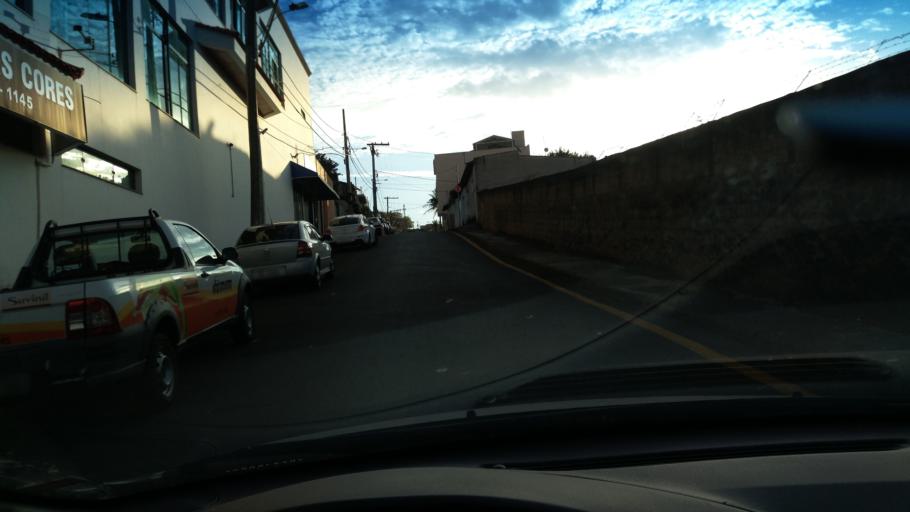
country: BR
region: Minas Gerais
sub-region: Andradas
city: Andradas
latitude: -22.0744
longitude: -46.5782
